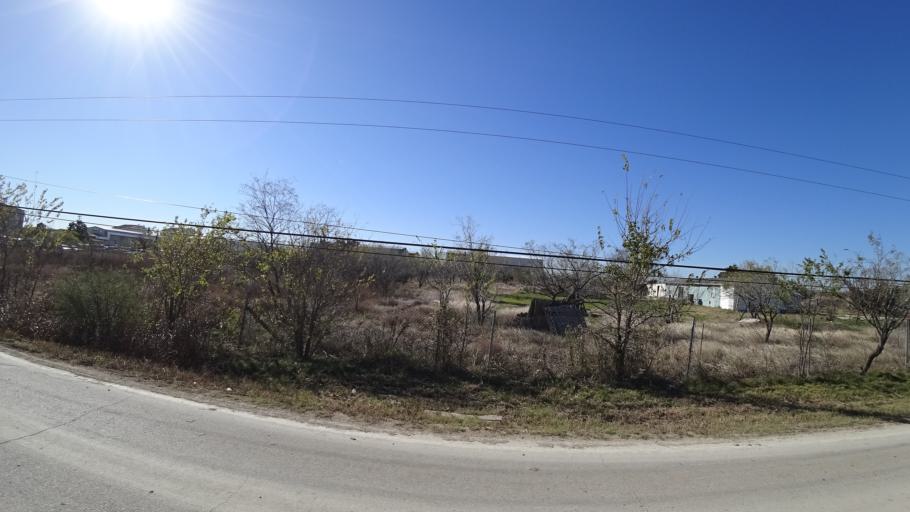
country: US
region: Texas
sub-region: Travis County
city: Onion Creek
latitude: 30.1214
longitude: -97.6668
